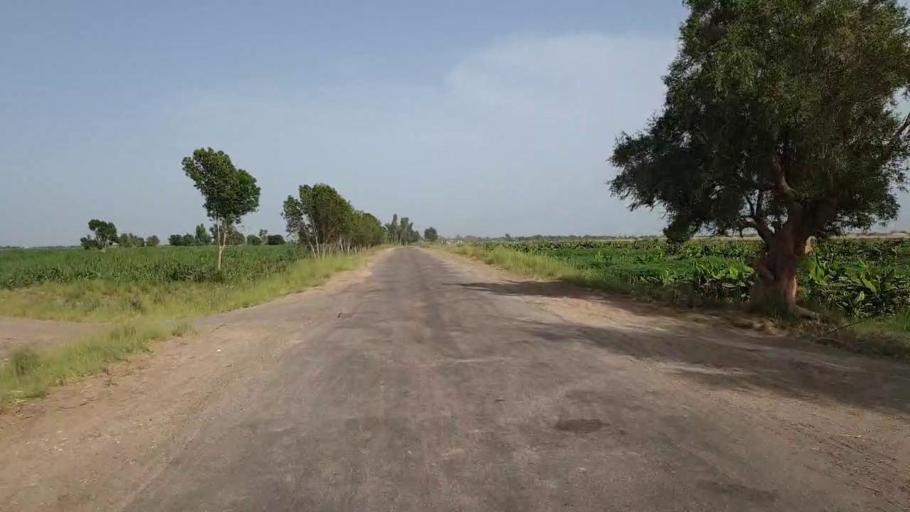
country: PK
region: Sindh
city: Sakrand
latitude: 26.2796
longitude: 68.2691
